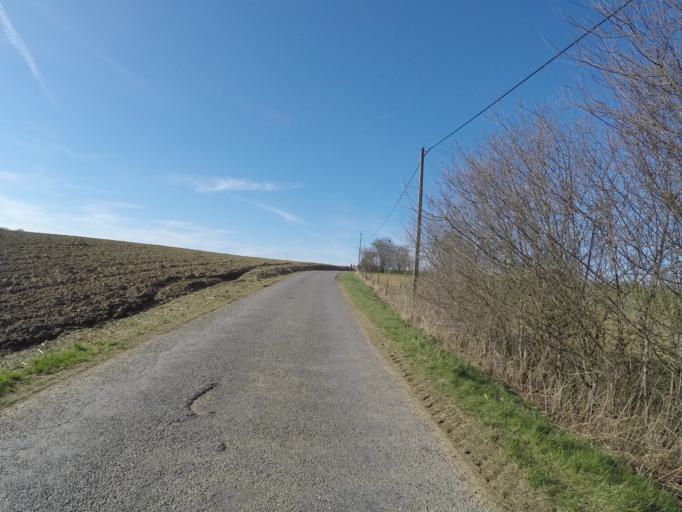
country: BE
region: Wallonia
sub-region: Province de Namur
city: Hamois
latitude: 50.3427
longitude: 5.1365
